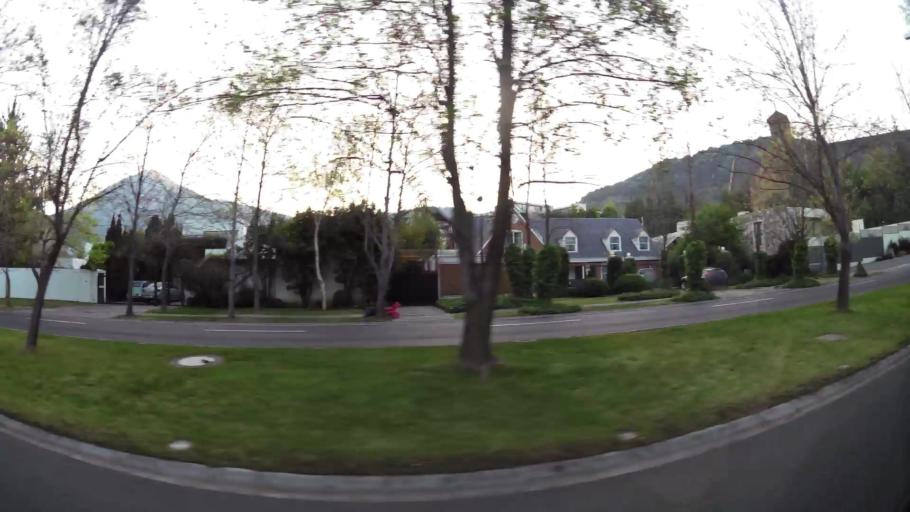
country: CL
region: Santiago Metropolitan
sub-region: Provincia de Chacabuco
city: Chicureo Abajo
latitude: -33.3377
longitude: -70.5540
